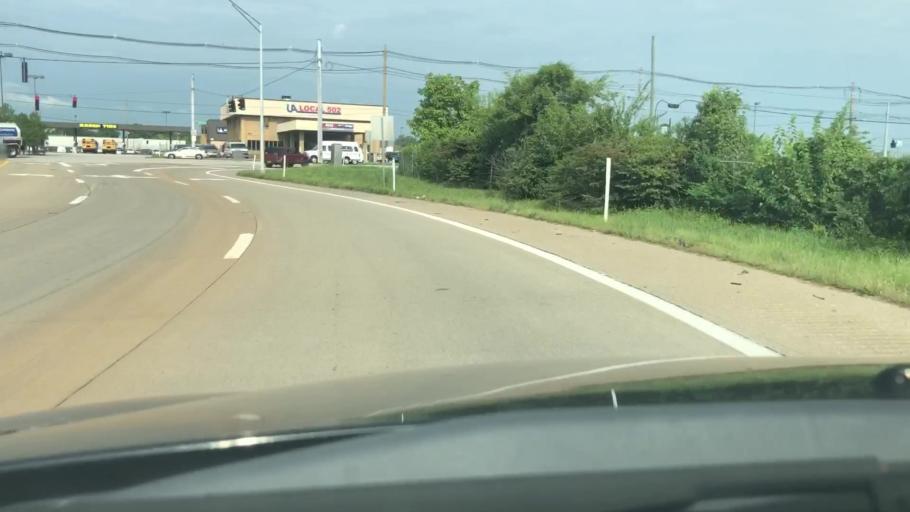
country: US
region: Kentucky
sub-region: Jefferson County
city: Audubon Park
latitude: 38.1915
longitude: -85.7499
